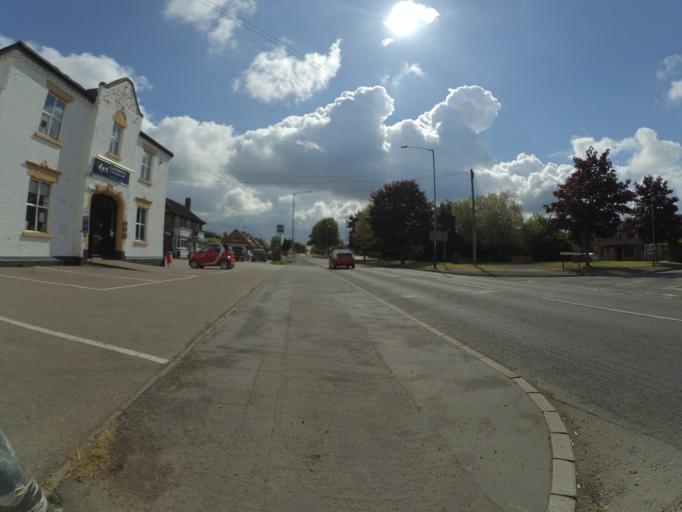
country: GB
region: England
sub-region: Warwickshire
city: Rugby
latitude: 52.3581
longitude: -1.2164
